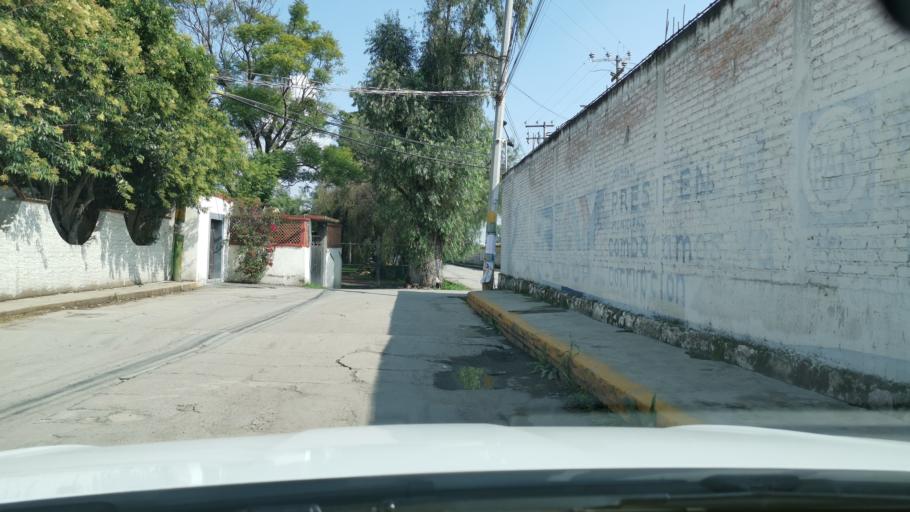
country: MX
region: Mexico
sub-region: Cuautitlan
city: San Jose del Puente
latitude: 19.7132
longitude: -99.1876
